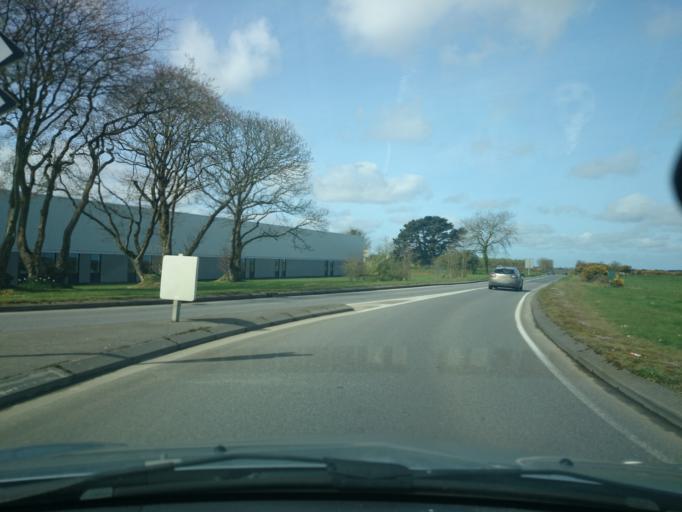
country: FR
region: Brittany
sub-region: Departement du Finistere
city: Guipavas
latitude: 48.4416
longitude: -4.4234
